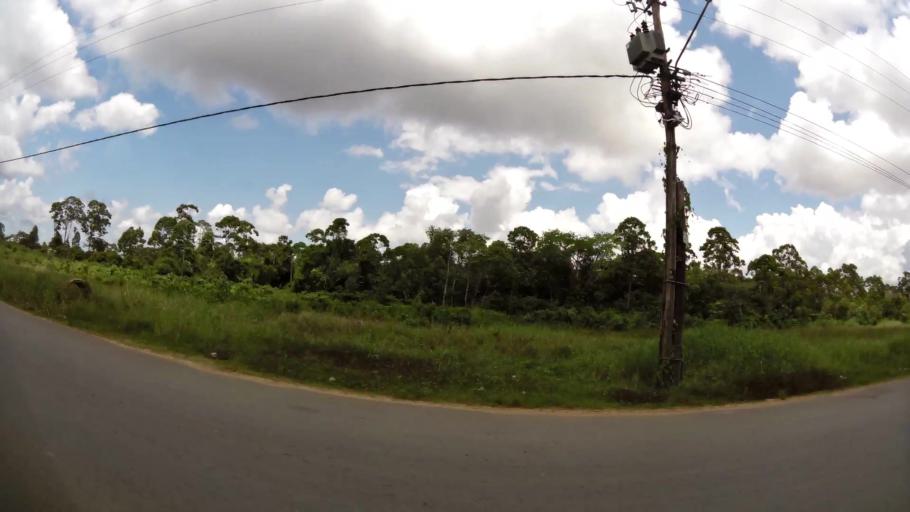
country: SR
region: Paramaribo
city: Paramaribo
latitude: 5.8025
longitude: -55.1240
